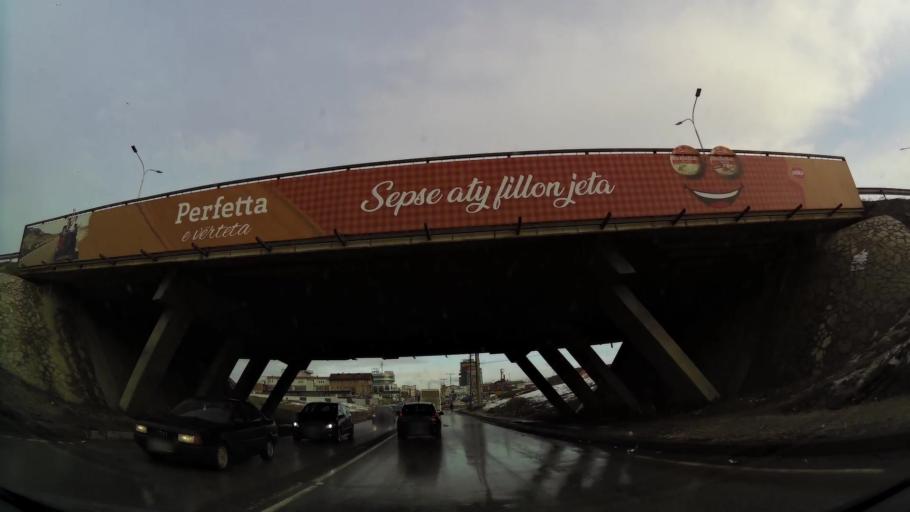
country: XK
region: Pristina
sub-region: Komuna e Prishtines
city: Pristina
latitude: 42.6310
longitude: 21.1500
